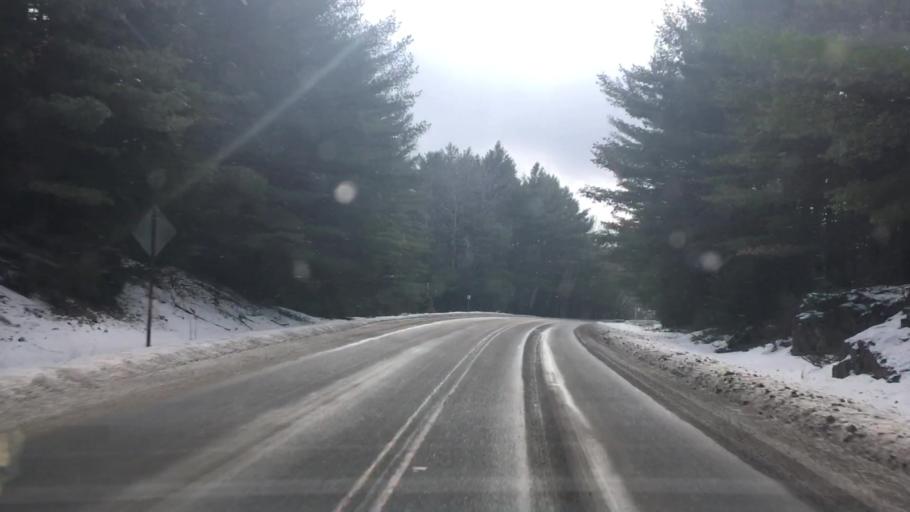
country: US
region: Maine
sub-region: Washington County
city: Calais
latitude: 45.0443
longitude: -67.3276
